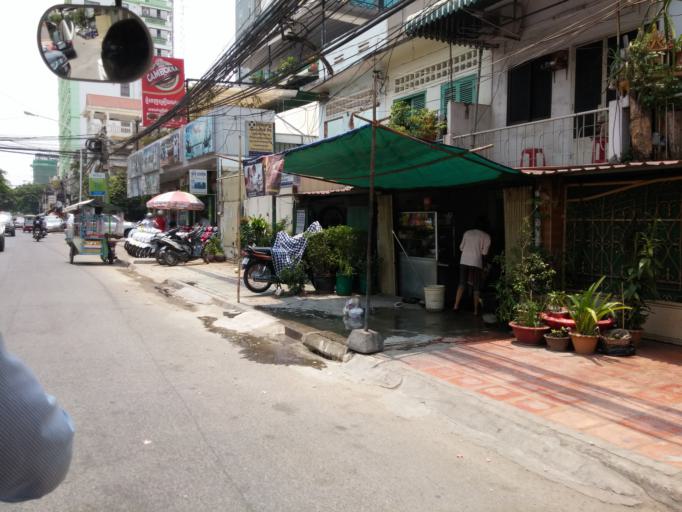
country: KH
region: Phnom Penh
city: Phnom Penh
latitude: 11.5577
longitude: 104.9191
